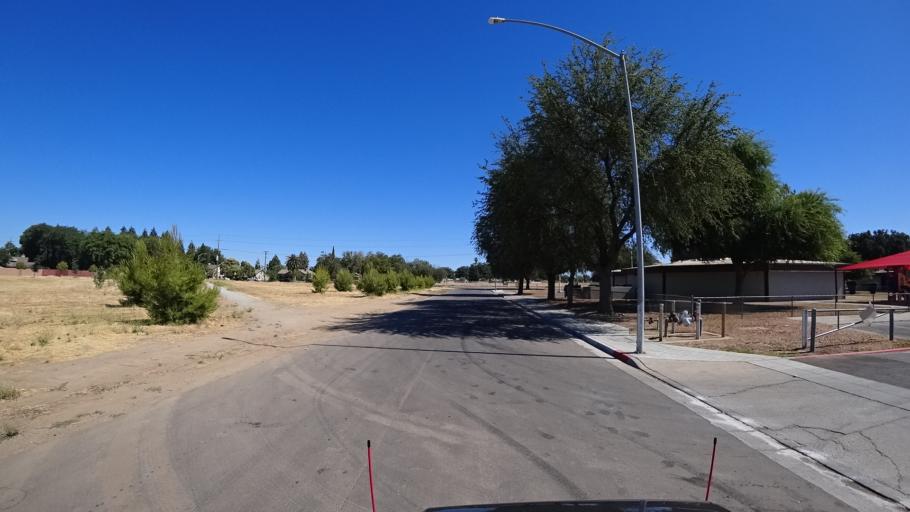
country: US
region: California
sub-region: Fresno County
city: Easton
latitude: 36.6985
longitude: -119.7964
